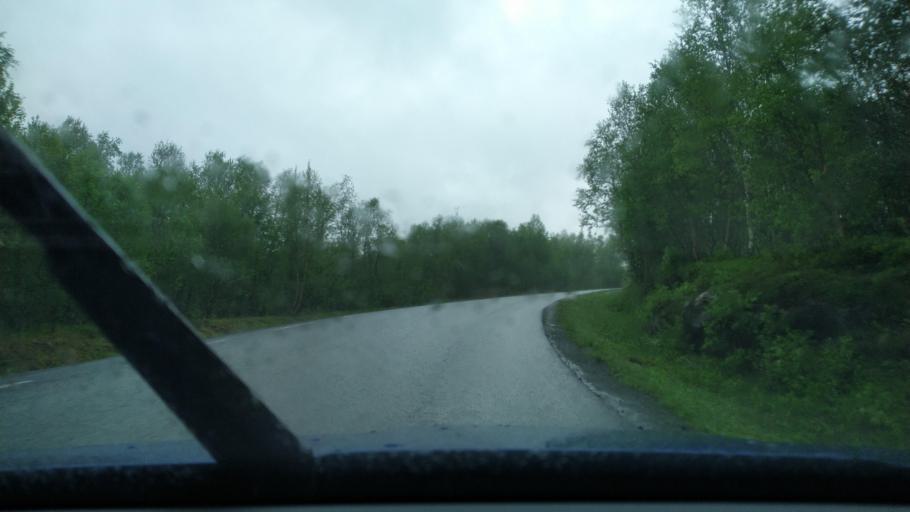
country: NO
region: Troms
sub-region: Dyroy
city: Brostadbotn
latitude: 69.0170
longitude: 17.7367
